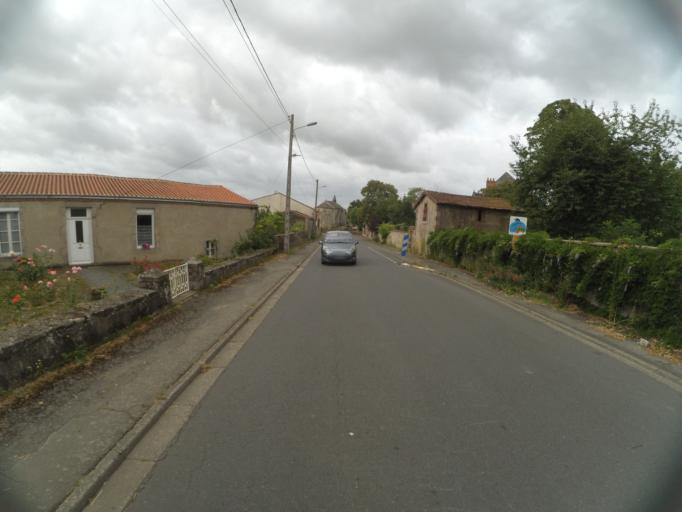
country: FR
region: Pays de la Loire
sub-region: Departement de Maine-et-Loire
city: Montfaucon-Montigne
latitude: 47.1011
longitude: -1.1216
